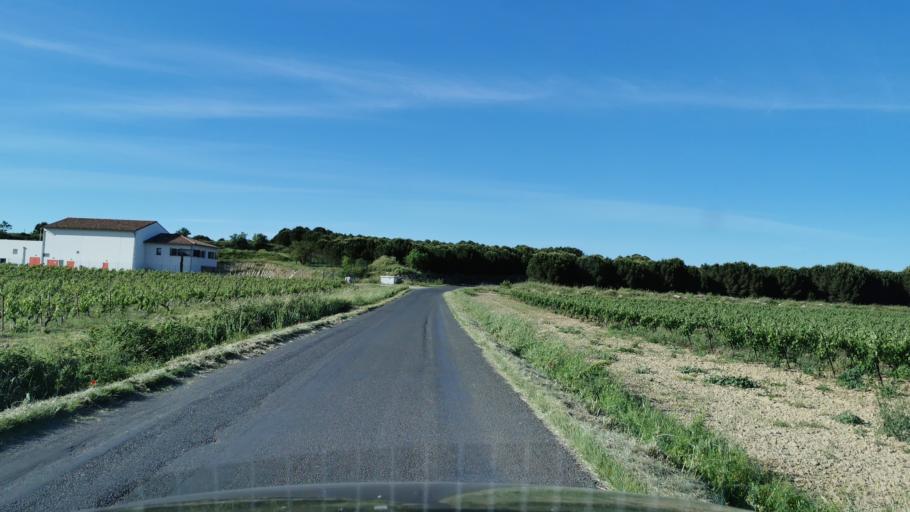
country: FR
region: Languedoc-Roussillon
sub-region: Departement de l'Aude
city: Nevian
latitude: 43.2175
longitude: 2.9127
